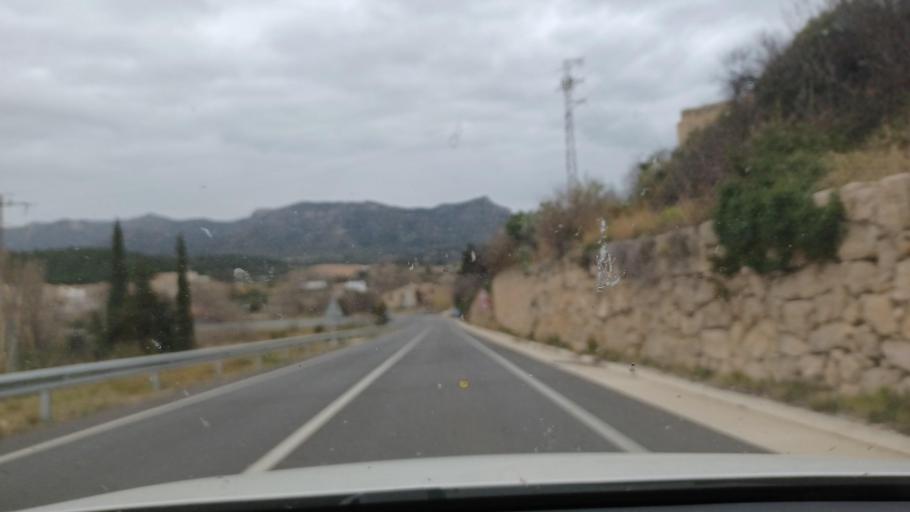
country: ES
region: Valencia
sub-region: Provincia de Castello
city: Rosell
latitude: 40.6327
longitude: 0.2795
